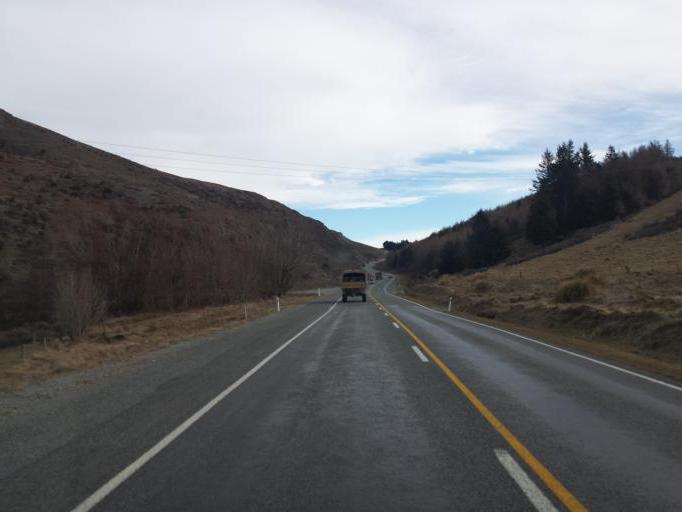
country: NZ
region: Canterbury
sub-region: Timaru District
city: Pleasant Point
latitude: -44.0915
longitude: 170.6163
